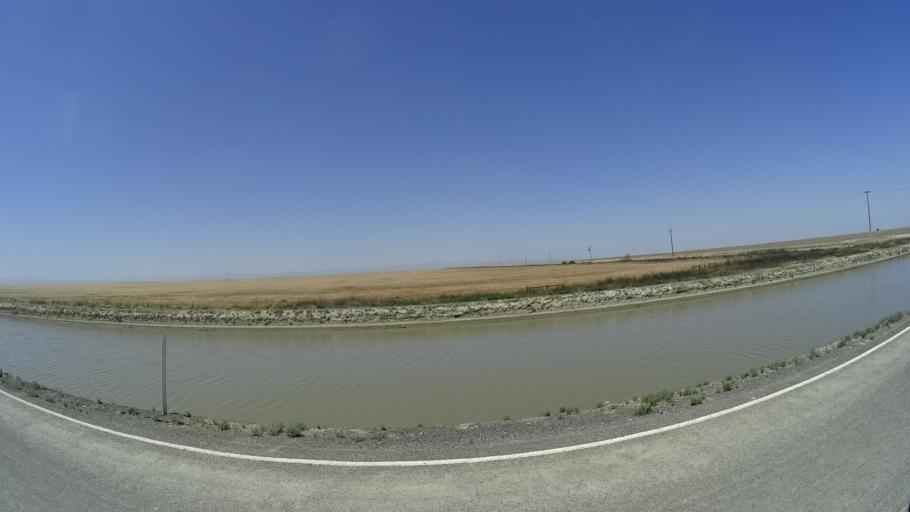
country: US
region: California
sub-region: Tulare County
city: Alpaugh
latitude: 35.9478
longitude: -119.6460
